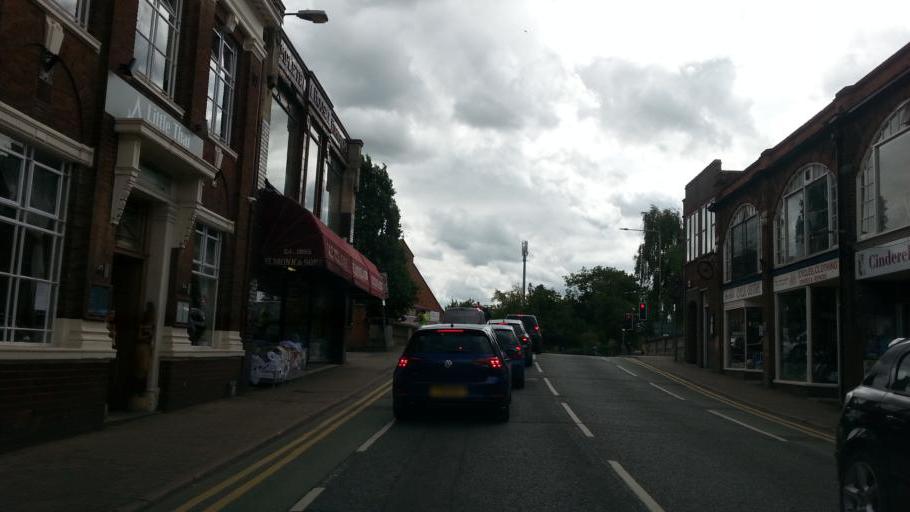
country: GB
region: England
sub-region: Leicestershire
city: Market Harborough
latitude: 52.4775
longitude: -0.9198
